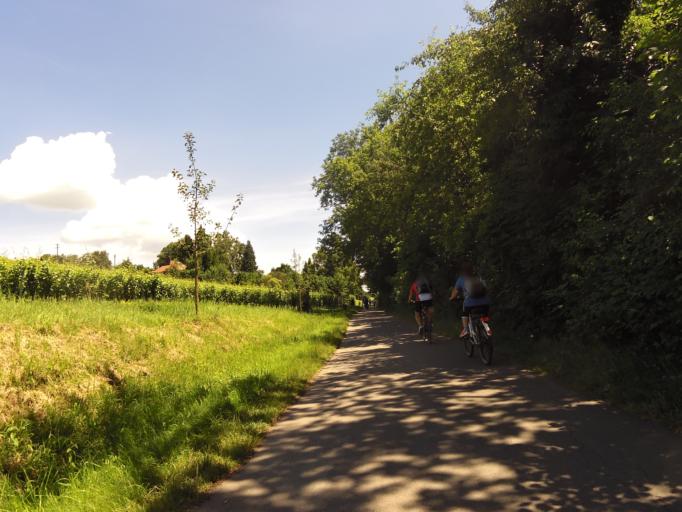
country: DE
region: Baden-Wuerttemberg
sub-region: Tuebingen Region
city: Stetten
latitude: 47.6816
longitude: 9.2934
